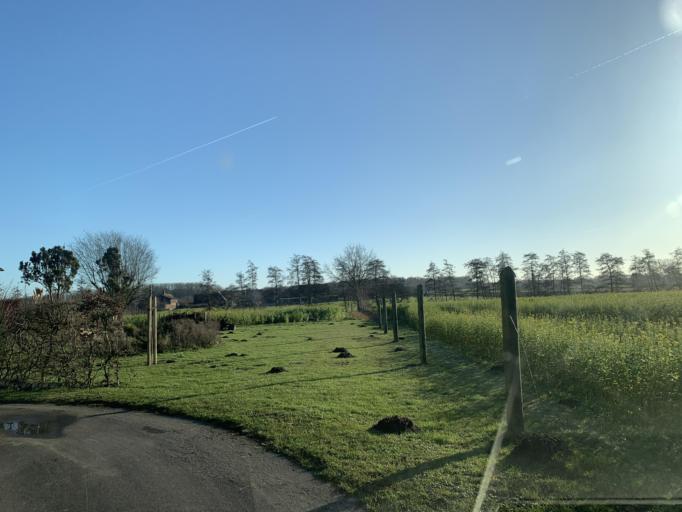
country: DE
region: North Rhine-Westphalia
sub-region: Regierungsbezirk Munster
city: Dulmen
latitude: 51.8534
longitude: 7.2972
